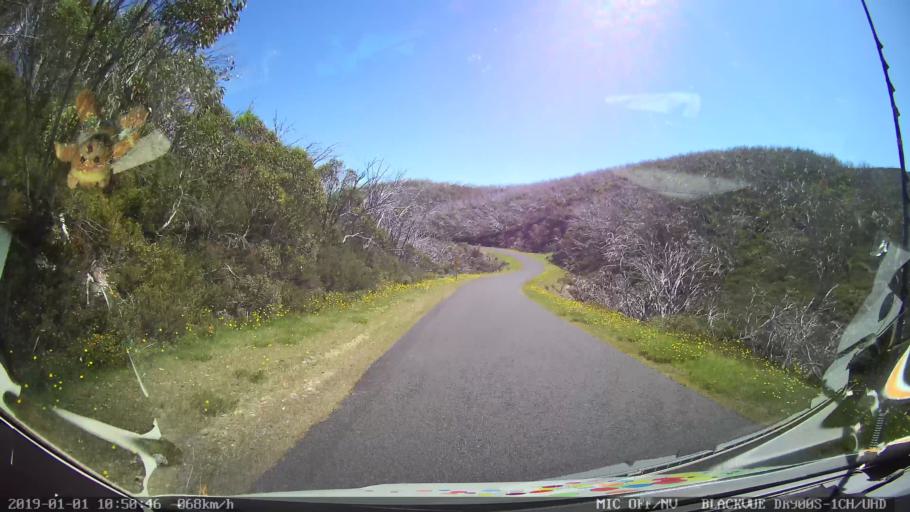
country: AU
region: New South Wales
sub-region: Snowy River
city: Jindabyne
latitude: -36.0253
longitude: 148.3716
